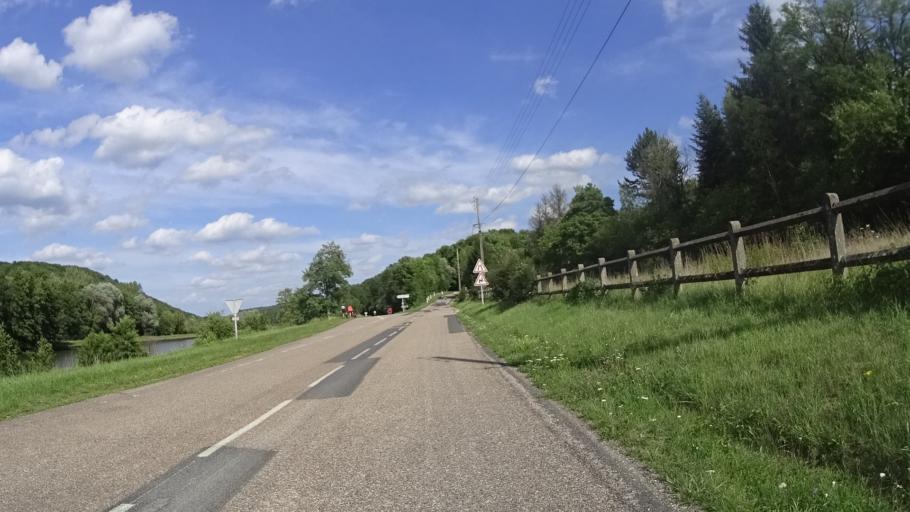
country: FR
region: Lorraine
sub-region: Departement de Meurthe-et-Moselle
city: Dommartin-les-Toul
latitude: 48.6430
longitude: 5.9421
